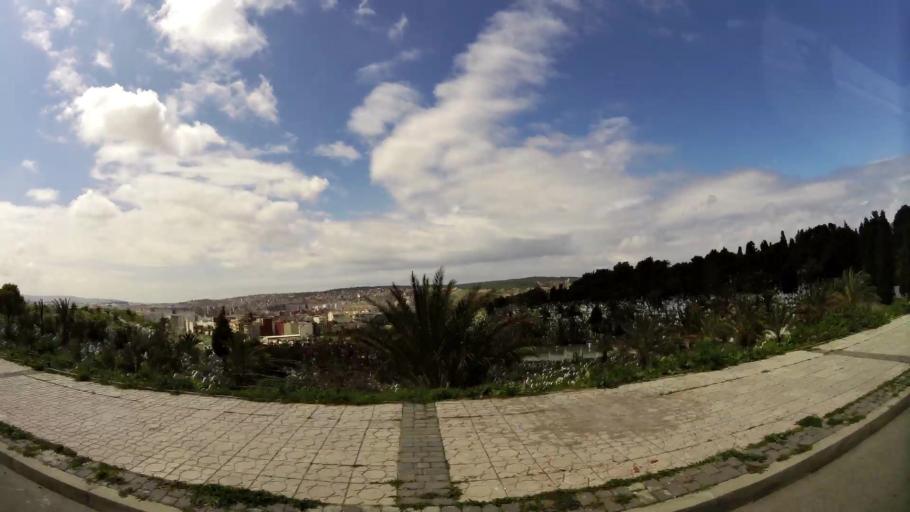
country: MA
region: Tanger-Tetouan
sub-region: Tanger-Assilah
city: Tangier
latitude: 35.7730
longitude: -5.8408
